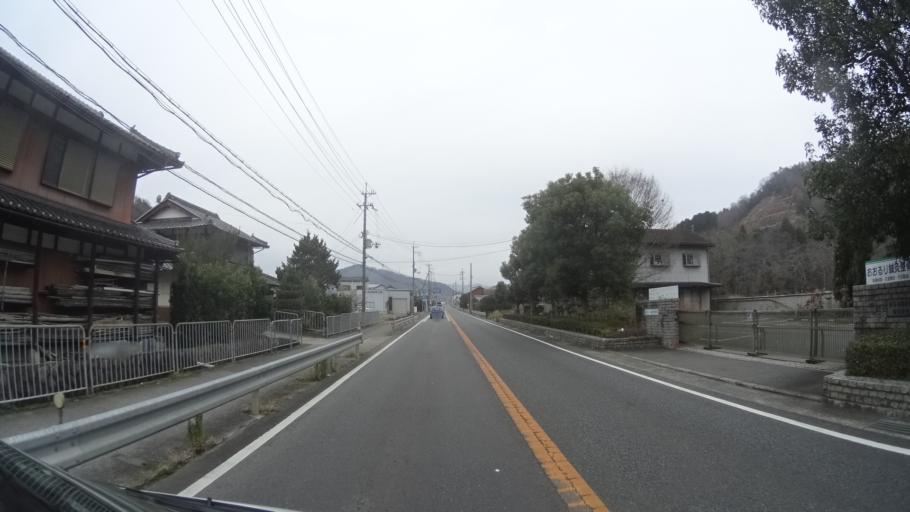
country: JP
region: Kyoto
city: Kameoka
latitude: 35.1000
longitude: 135.4912
